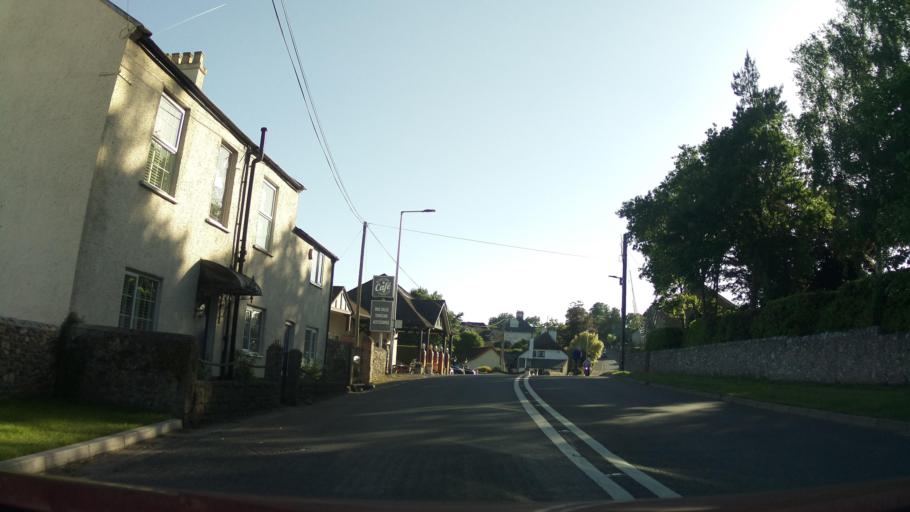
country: GB
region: England
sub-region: Devon
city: Colyton
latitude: 50.7281
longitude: -3.0603
